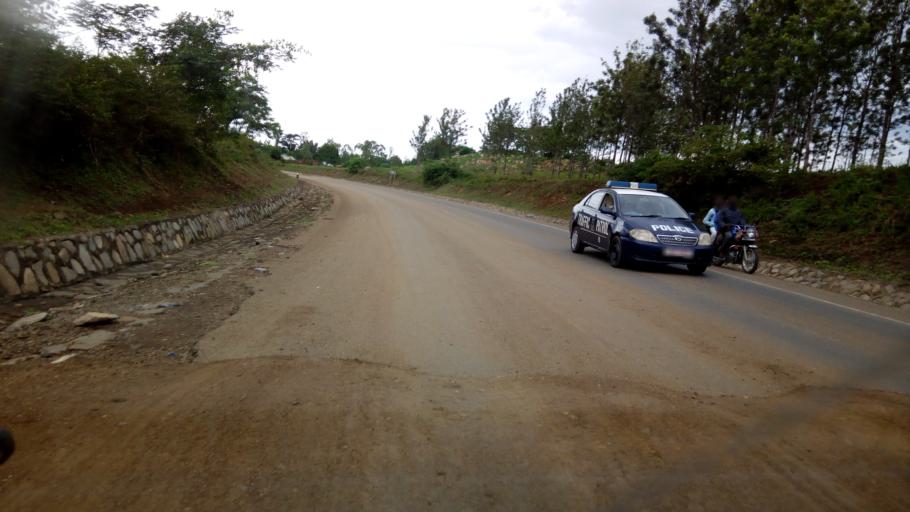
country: UG
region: Eastern Region
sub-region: Mbale District
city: Mbale
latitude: 0.9349
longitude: 34.1571
